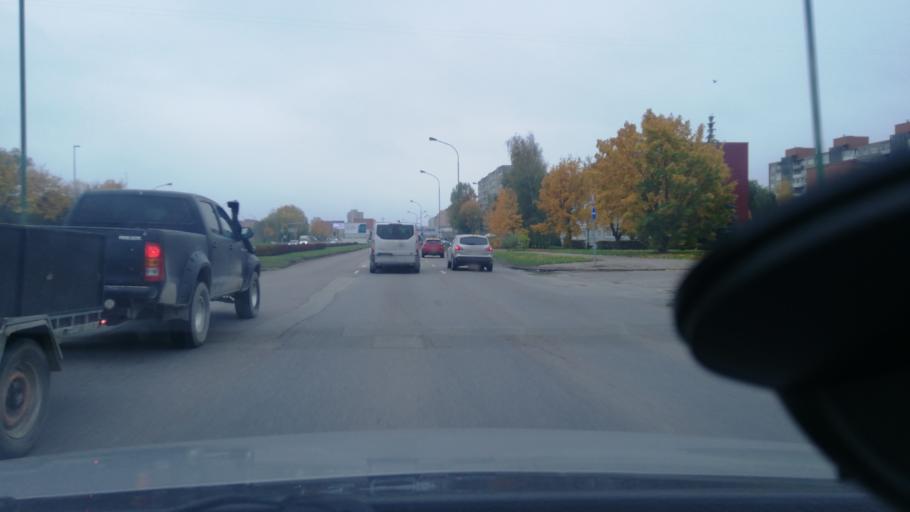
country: LT
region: Klaipedos apskritis
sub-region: Klaipeda
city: Klaipeda
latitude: 55.6811
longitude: 21.1864
